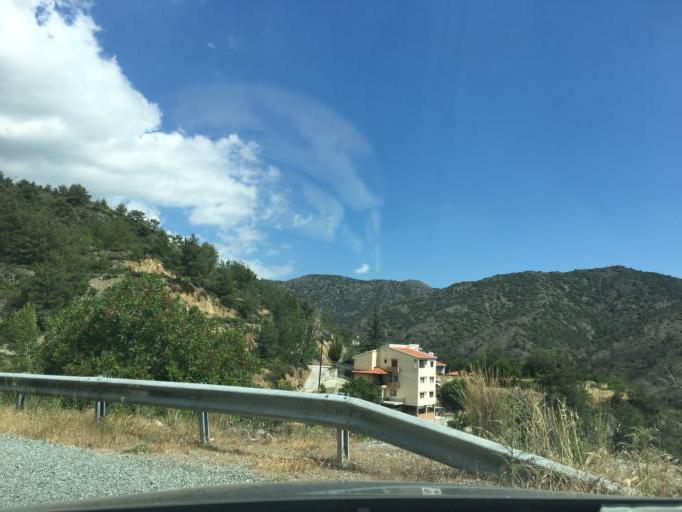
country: CY
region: Limassol
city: Pelendri
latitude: 34.9005
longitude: 33.0160
